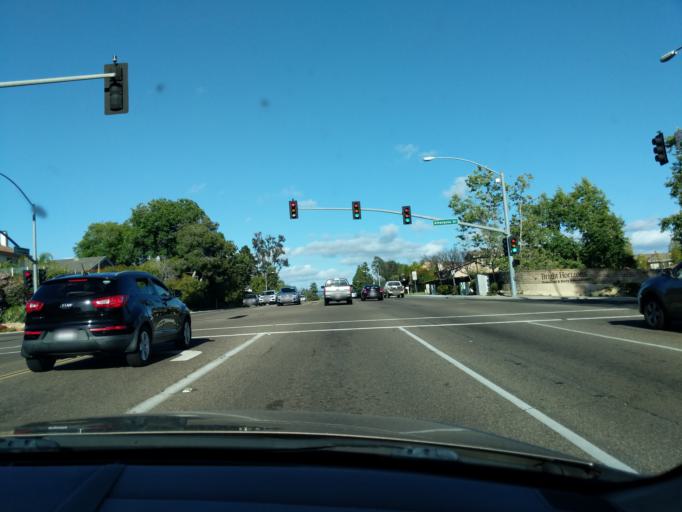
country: US
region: California
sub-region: San Diego County
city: Encinitas
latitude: 33.0671
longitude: -117.2554
